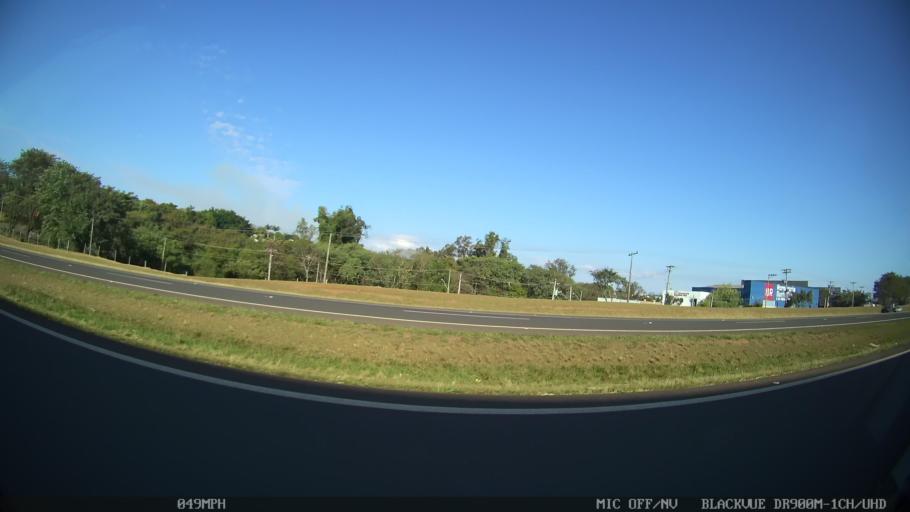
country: BR
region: Sao Paulo
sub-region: Piracicaba
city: Piracicaba
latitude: -22.6753
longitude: -47.6320
